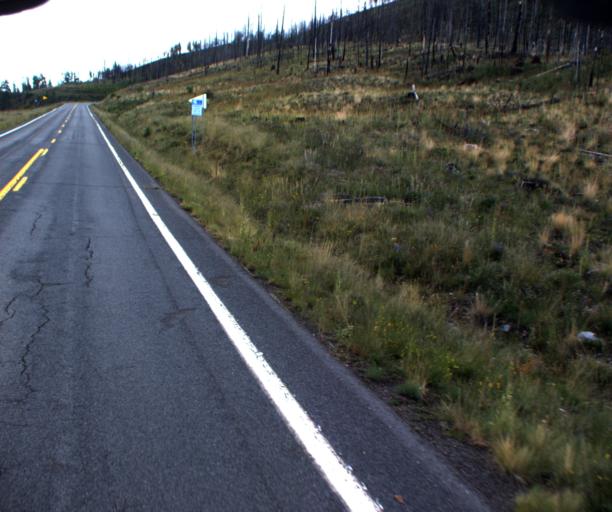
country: US
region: Arizona
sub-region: Apache County
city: Eagar
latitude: 34.0474
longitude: -109.3602
